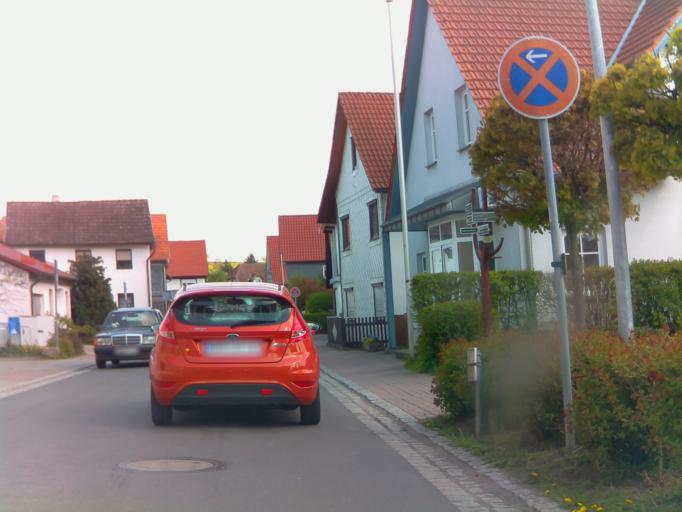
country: DE
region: Thuringia
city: Westhausen
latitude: 50.3536
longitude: 10.6845
